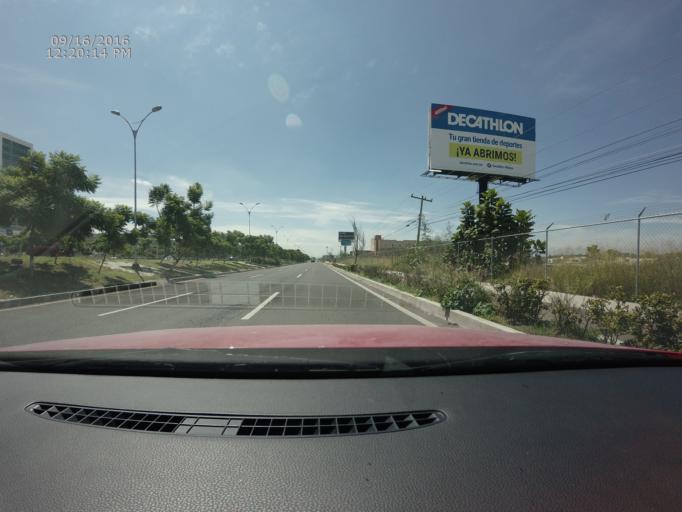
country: MX
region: Queretaro
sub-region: Queretaro
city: El Salitre
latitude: 20.6646
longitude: -100.4333
